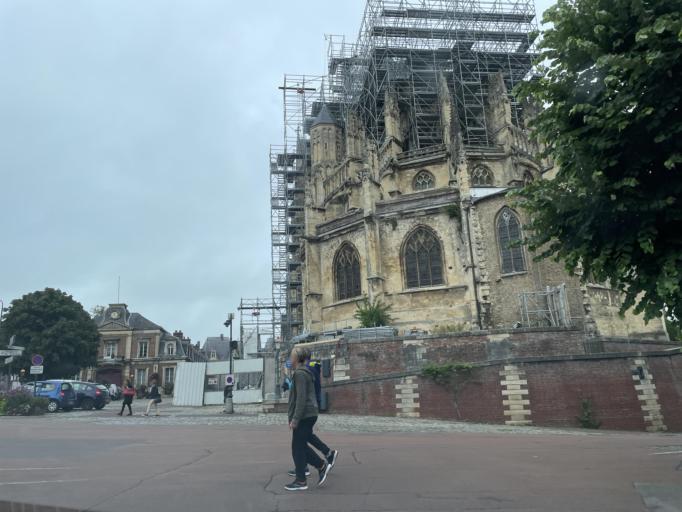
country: FR
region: Haute-Normandie
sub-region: Departement de la Seine-Maritime
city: Eu
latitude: 50.0484
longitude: 1.4203
